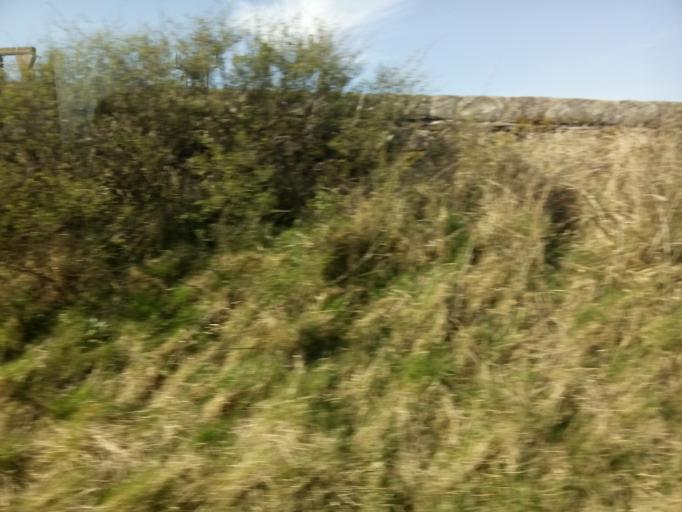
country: GB
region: England
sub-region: Northumberland
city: Berwick-Upon-Tweed
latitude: 55.8014
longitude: -2.0276
